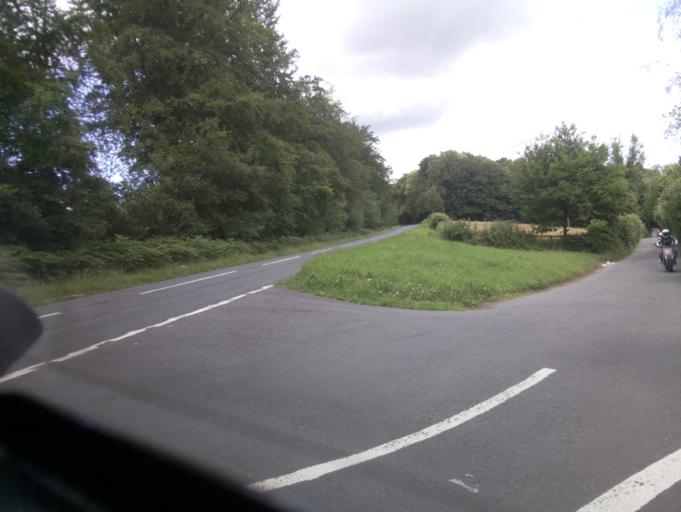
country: GB
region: England
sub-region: Gloucestershire
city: Bream
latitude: 51.7373
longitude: -2.5531
